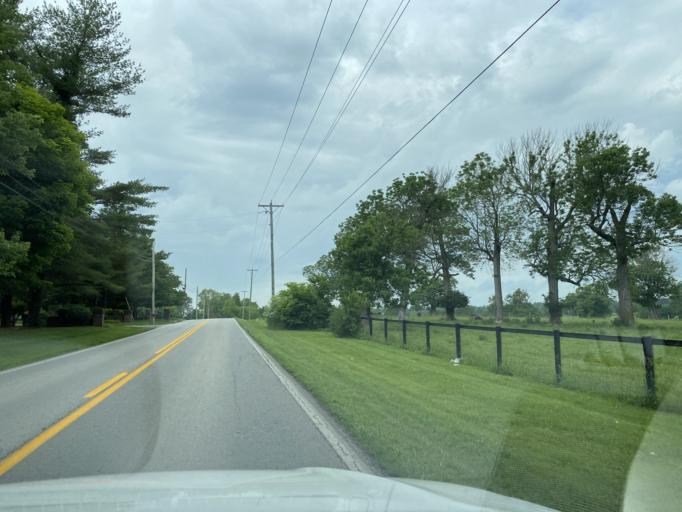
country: US
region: Kentucky
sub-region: Scott County
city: Georgetown
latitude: 38.2191
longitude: -84.4916
